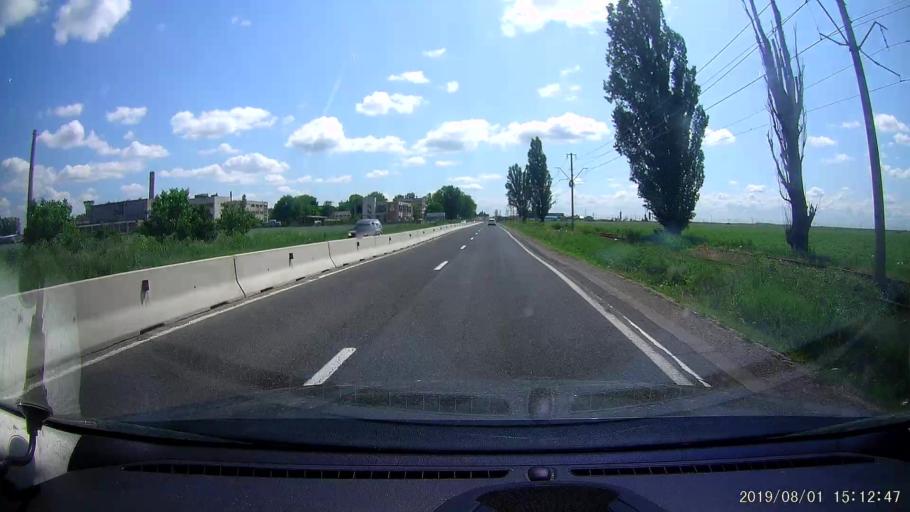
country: RO
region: Braila
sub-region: Comuna Chiscani
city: Lacu Sarat
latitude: 45.2014
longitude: 27.9083
